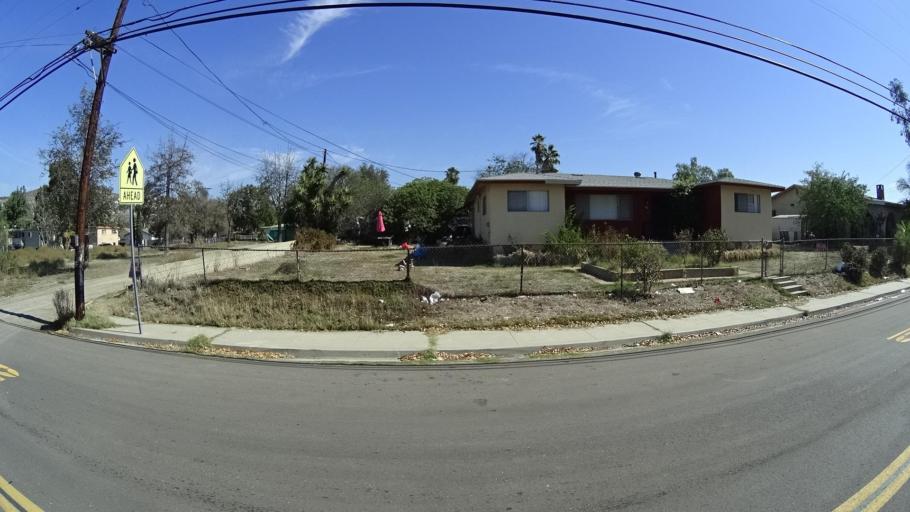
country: US
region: California
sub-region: San Diego County
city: La Presa
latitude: 32.7117
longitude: -117.0075
